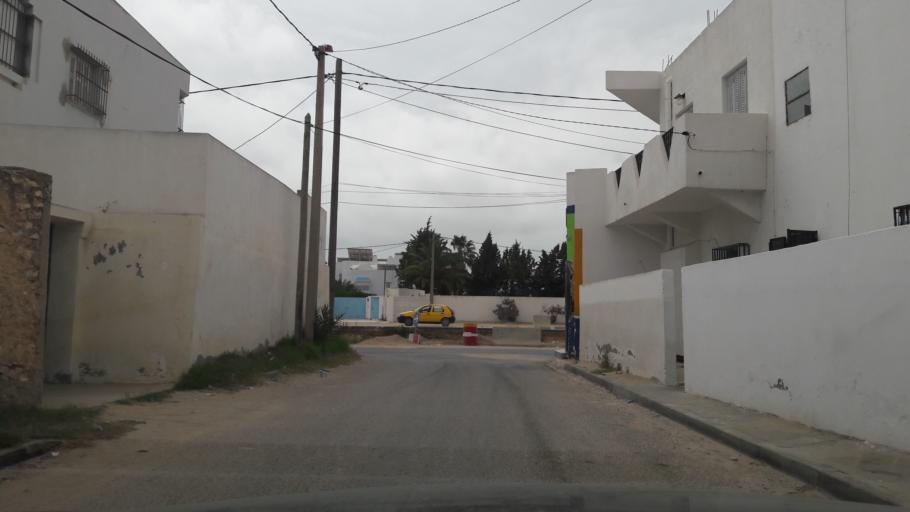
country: TN
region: Safaqis
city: Sfax
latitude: 34.7713
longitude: 10.7566
